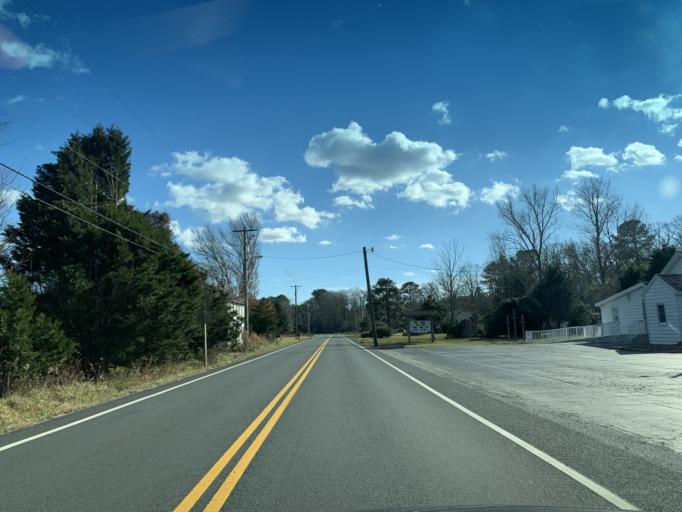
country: US
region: Maryland
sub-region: Worcester County
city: Berlin
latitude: 38.3635
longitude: -75.2010
